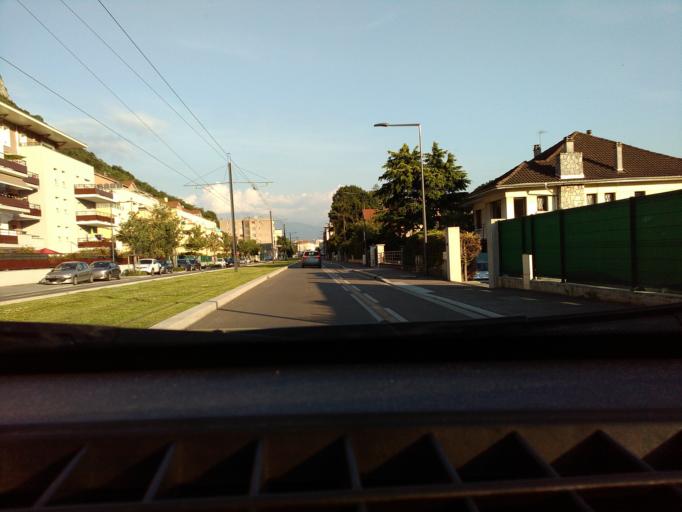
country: FR
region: Rhone-Alpes
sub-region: Departement de l'Isere
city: Saint-Egreve
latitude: 45.2197
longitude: 5.6918
